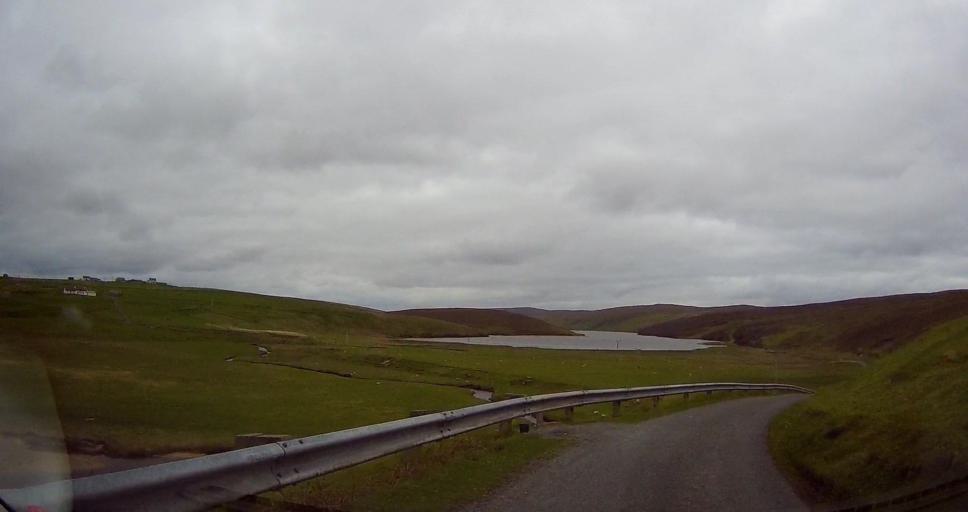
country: GB
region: Scotland
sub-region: Shetland Islands
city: Shetland
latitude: 60.8058
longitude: -0.8813
